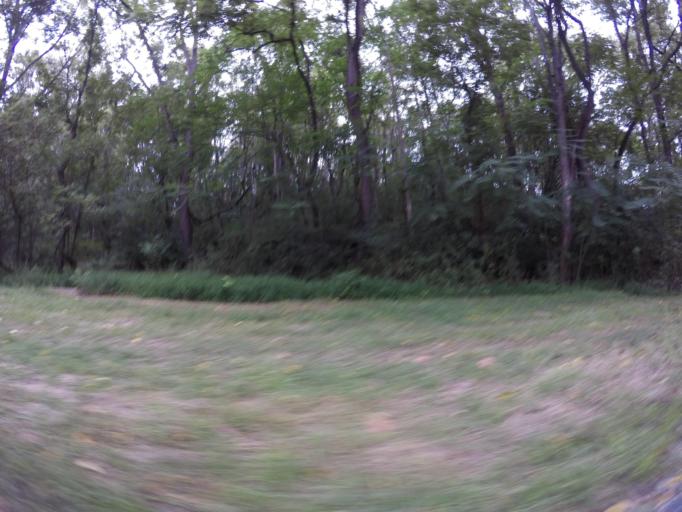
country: US
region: Maryland
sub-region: Carroll County
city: Sykesville
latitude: 39.3175
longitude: -77.0537
